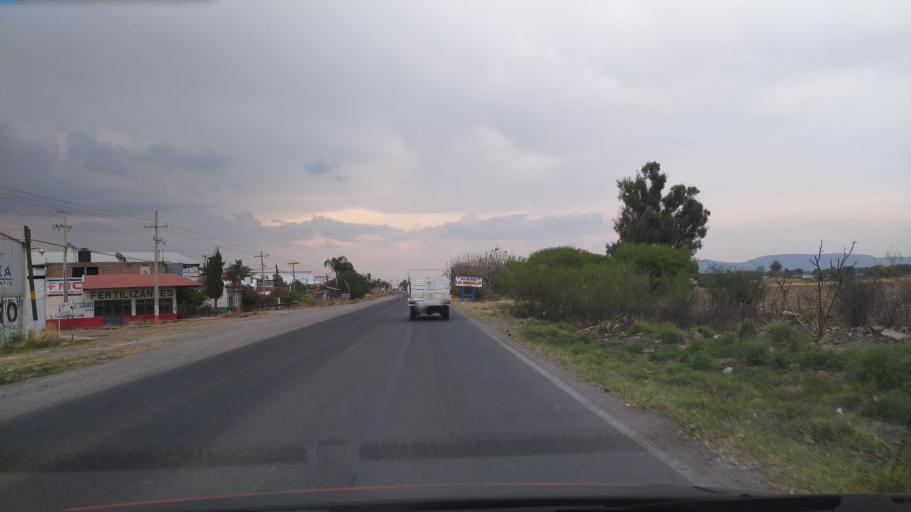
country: MX
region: Guanajuato
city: Ciudad Manuel Doblado
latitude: 20.7369
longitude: -101.9343
